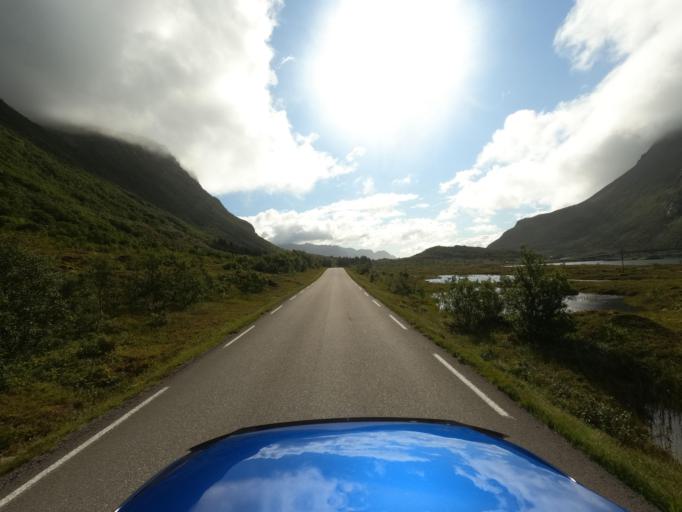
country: NO
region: Nordland
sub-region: Vagan
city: Kabelvag
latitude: 68.2750
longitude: 14.1644
